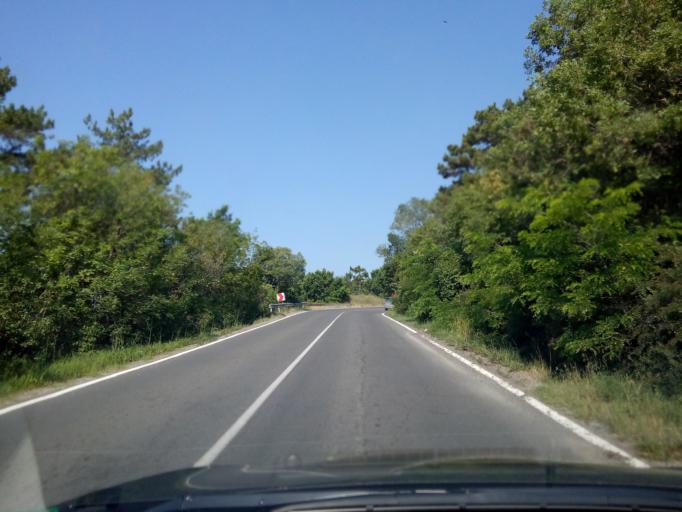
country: BG
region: Burgas
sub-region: Obshtina Nesebur
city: Sveti Vlas
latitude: 42.7252
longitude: 27.7384
